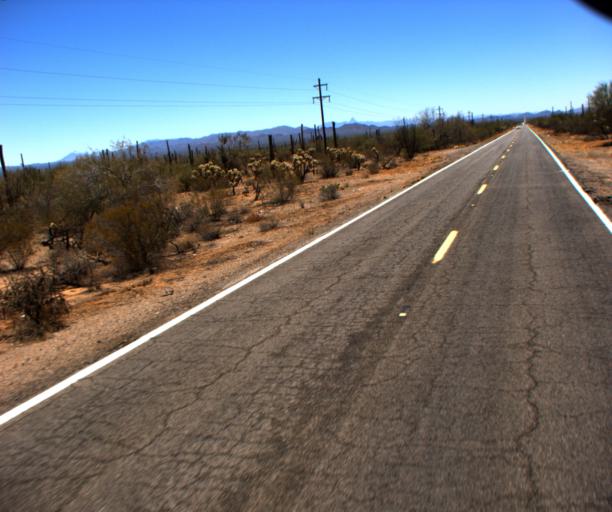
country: US
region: Arizona
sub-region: Pima County
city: Sells
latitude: 32.1313
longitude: -112.0906
